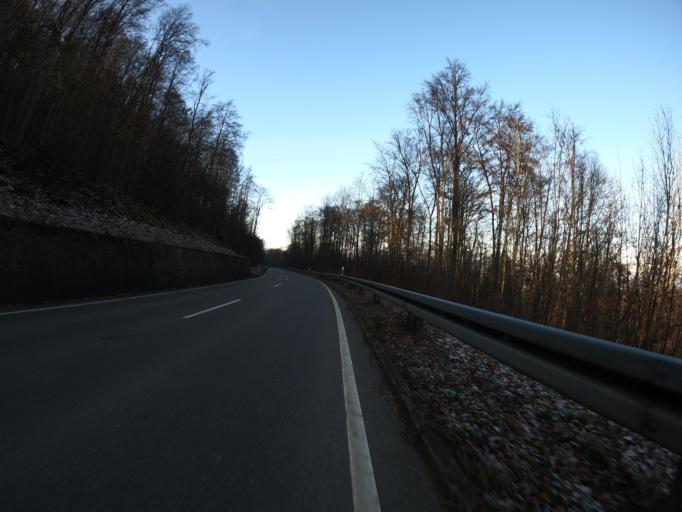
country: DE
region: Baden-Wuerttemberg
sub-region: Regierungsbezirk Stuttgart
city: Eschenbach
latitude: 48.6284
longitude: 9.6725
